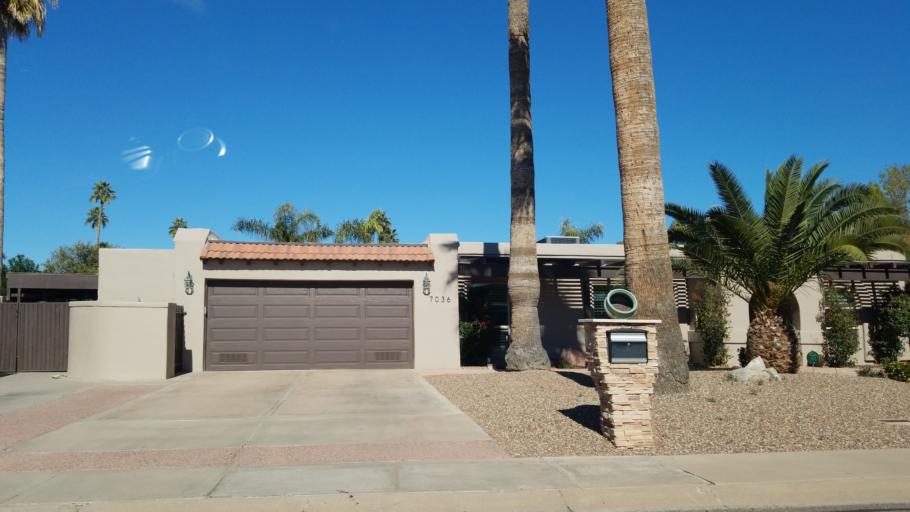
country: US
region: Arizona
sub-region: Maricopa County
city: Paradise Valley
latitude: 33.6127
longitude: -111.9286
